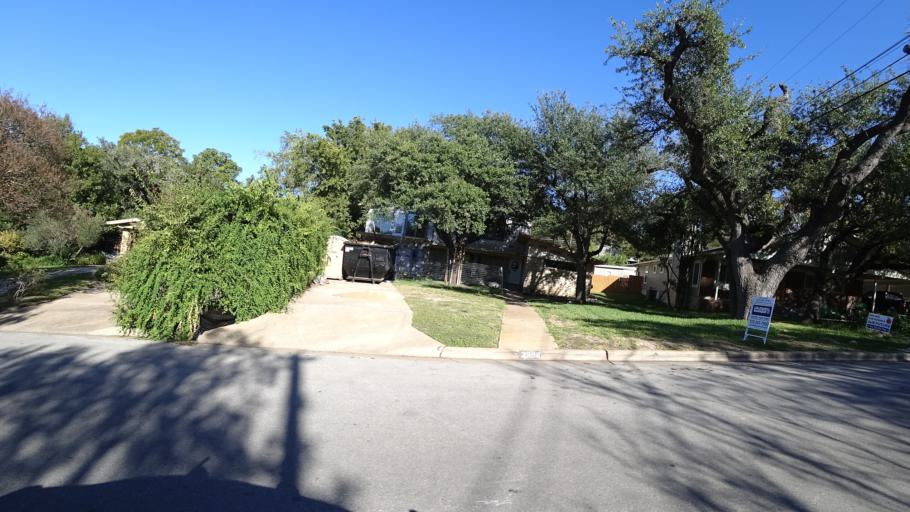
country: US
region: Texas
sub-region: Travis County
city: Rollingwood
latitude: 30.2447
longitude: -97.7858
